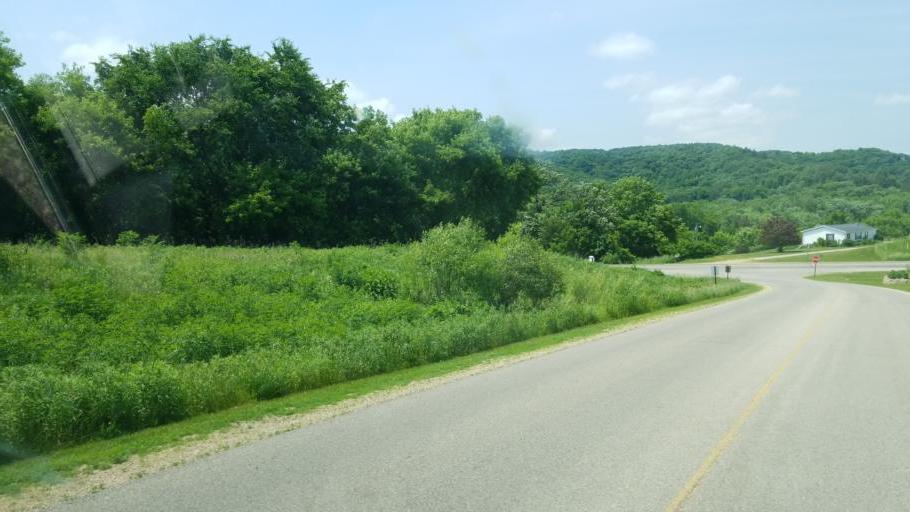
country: US
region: Wisconsin
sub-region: Monroe County
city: Cashton
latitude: 43.5821
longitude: -90.6385
